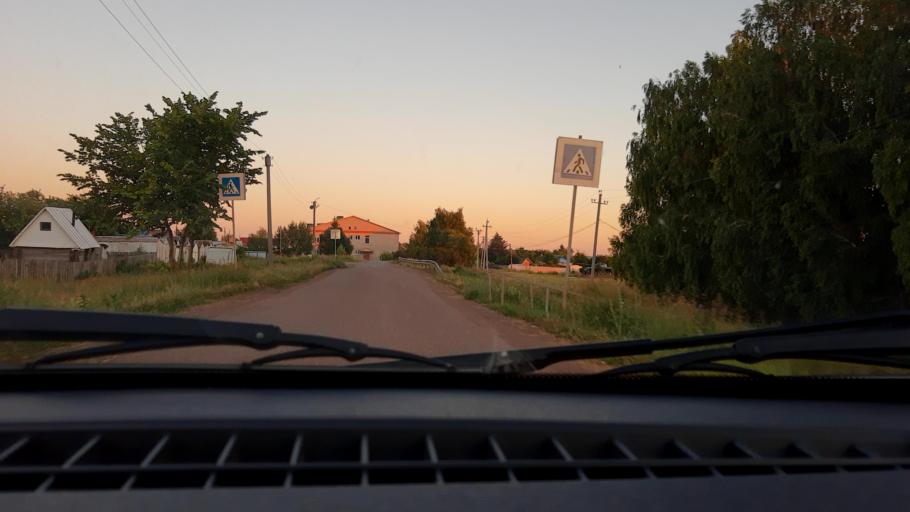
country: RU
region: Bashkortostan
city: Asanovo
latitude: 54.8899
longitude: 55.6240
